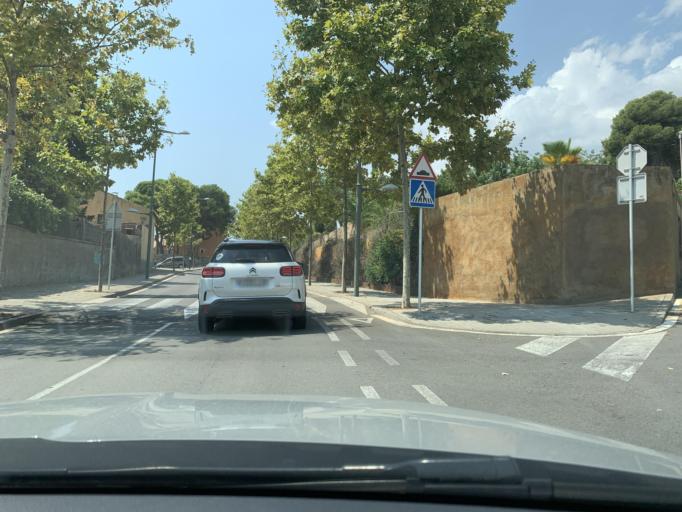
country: ES
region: Catalonia
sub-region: Provincia de Tarragona
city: Altafulla
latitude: 41.1408
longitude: 1.3799
